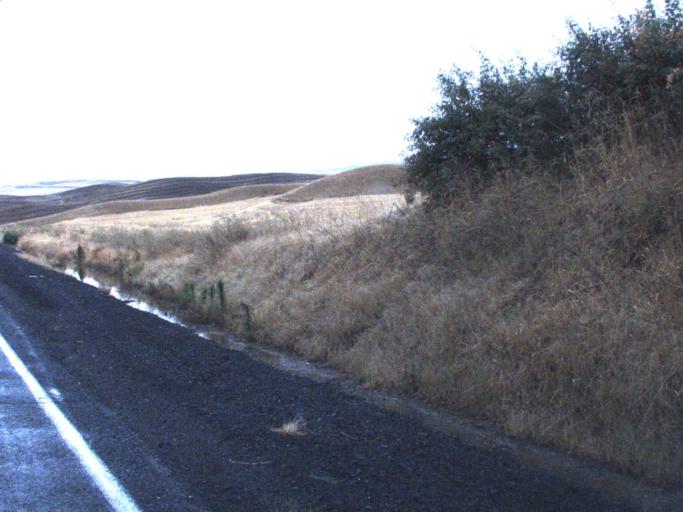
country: US
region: Washington
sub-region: Whitman County
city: Colfax
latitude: 47.0045
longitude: -117.3756
